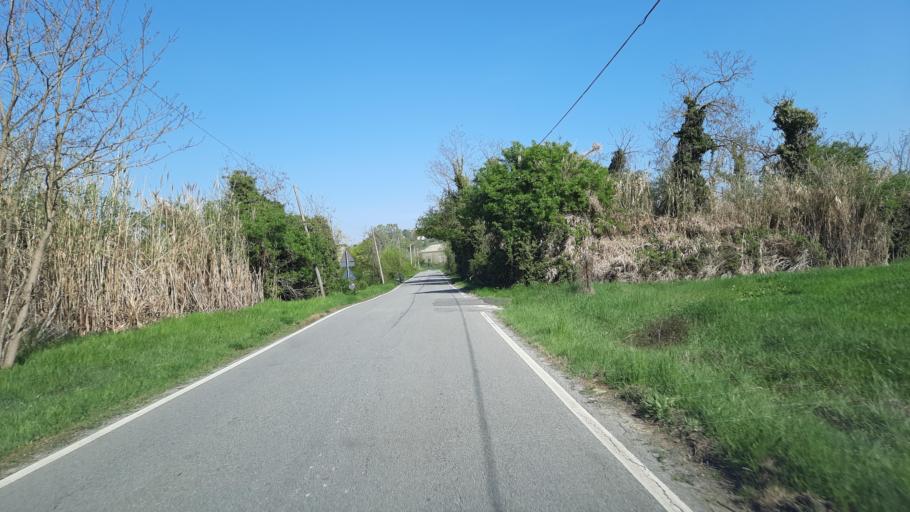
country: IT
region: Piedmont
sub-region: Provincia di Alessandria
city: Altavilla Monferrato
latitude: 45.0115
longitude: 8.3788
